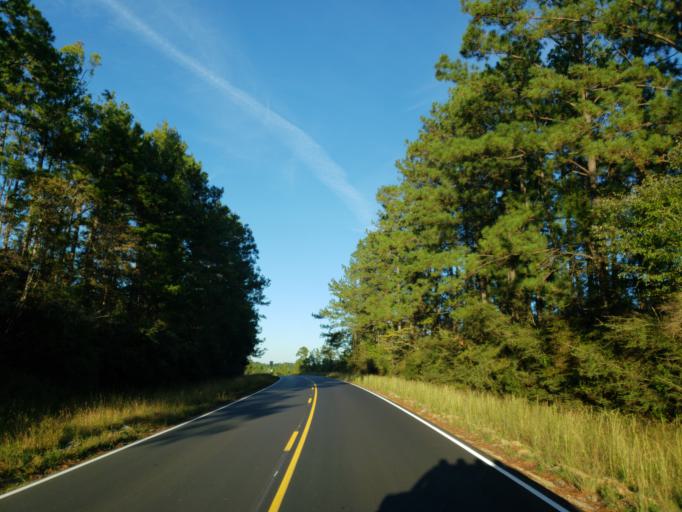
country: US
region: Mississippi
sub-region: Wayne County
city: Belmont
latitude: 31.4185
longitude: -88.5763
